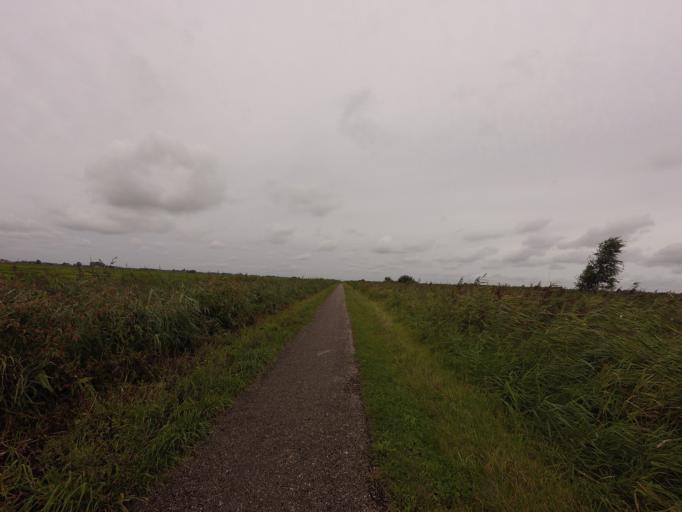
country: NL
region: Overijssel
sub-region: Gemeente Steenwijkerland
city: Blokzijl
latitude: 52.7738
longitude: 5.9100
